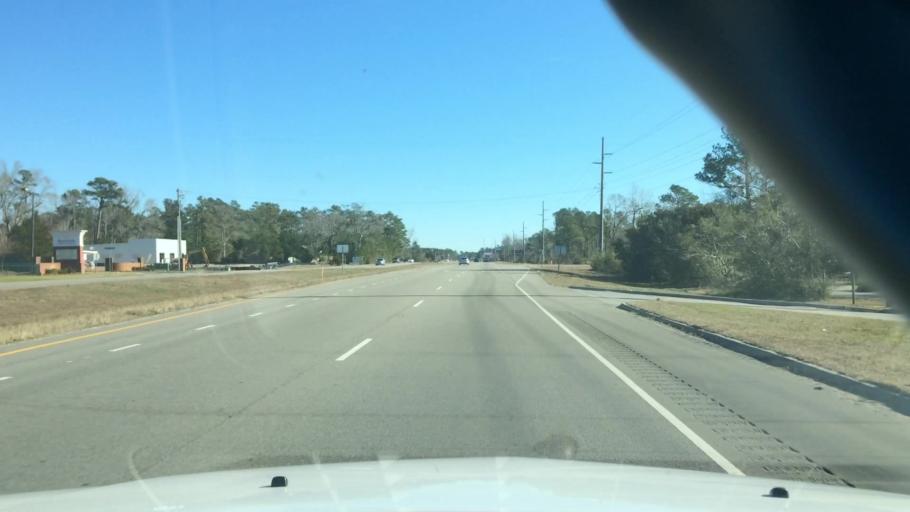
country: US
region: North Carolina
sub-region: Brunswick County
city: Shallotte
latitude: 34.0137
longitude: -78.2828
